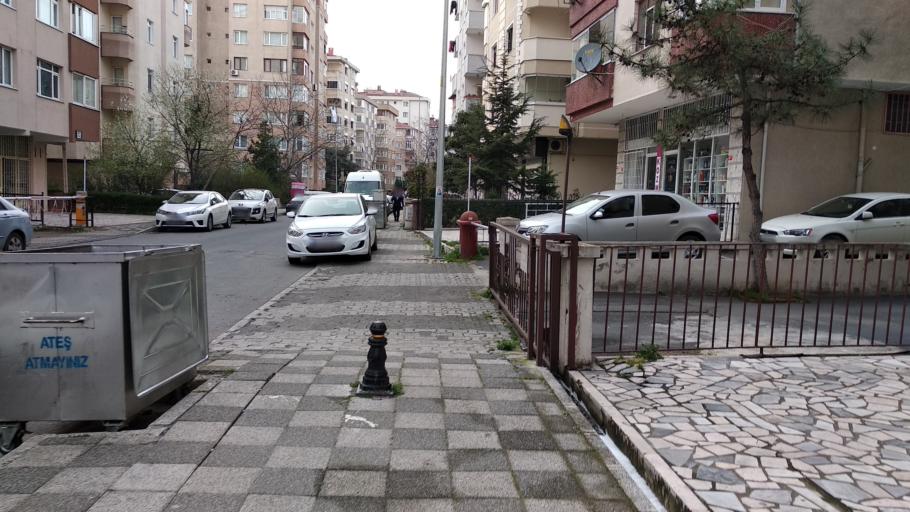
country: TR
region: Istanbul
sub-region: Atasehir
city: Atasehir
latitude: 40.9708
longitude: 29.1162
